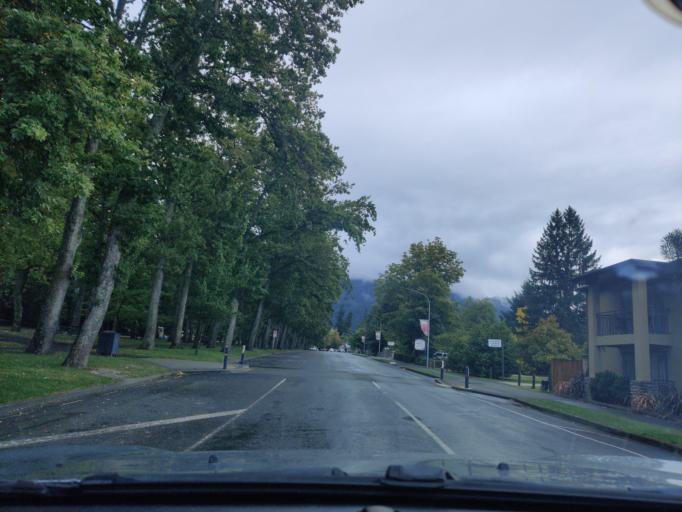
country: NZ
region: Canterbury
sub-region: Hurunui District
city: Amberley
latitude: -42.5253
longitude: 172.8291
